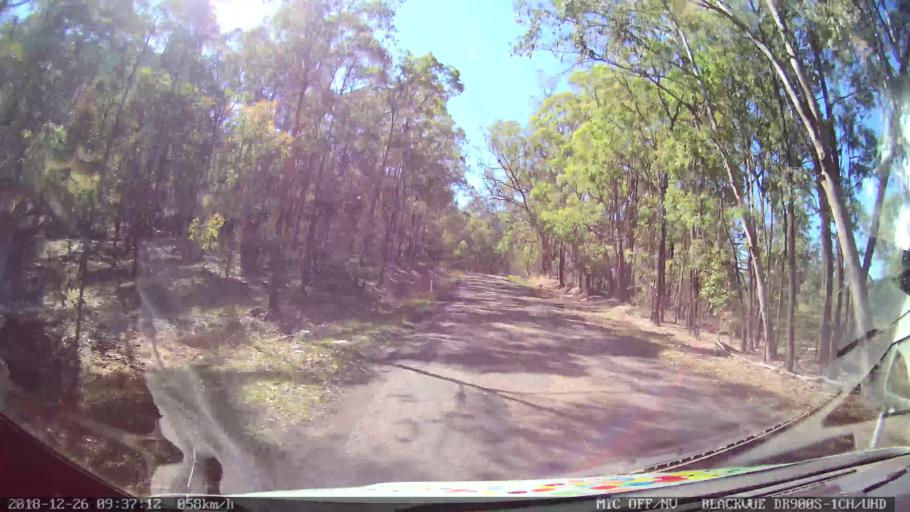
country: AU
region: New South Wales
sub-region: Mid-Western Regional
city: Kandos
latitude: -32.9306
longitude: 150.0392
